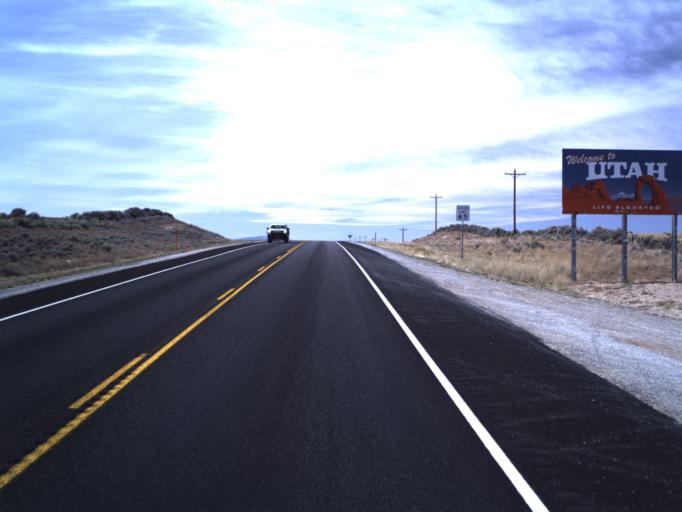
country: US
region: Colorado
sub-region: Dolores County
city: Dove Creek
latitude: 37.8166
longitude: -109.0424
